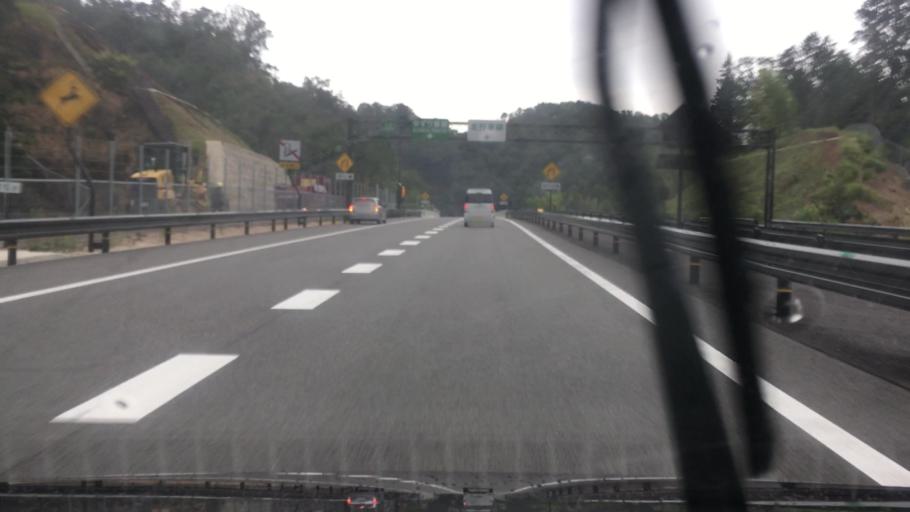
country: JP
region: Hyogo
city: Toyooka
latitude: 35.4303
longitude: 134.7673
